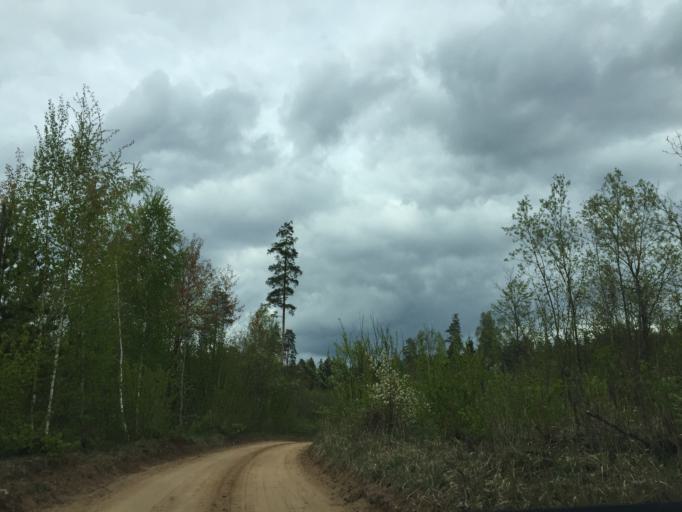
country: LV
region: Kekava
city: Kekava
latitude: 56.8052
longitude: 24.2988
